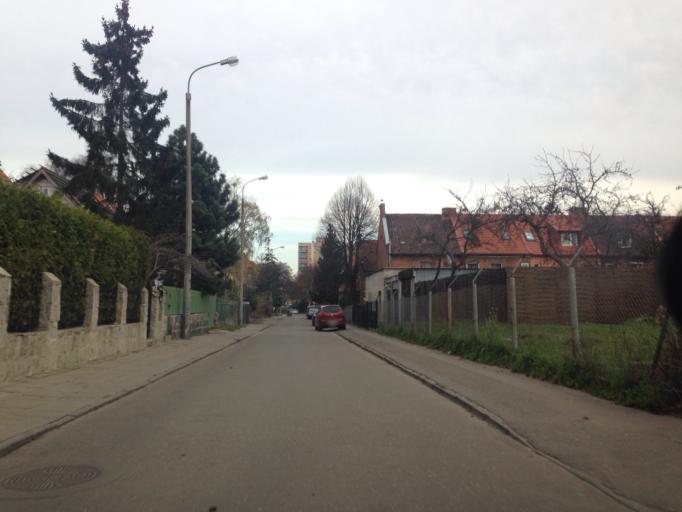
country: PL
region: Pomeranian Voivodeship
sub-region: Gdansk
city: Gdansk
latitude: 54.3856
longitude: 18.6193
